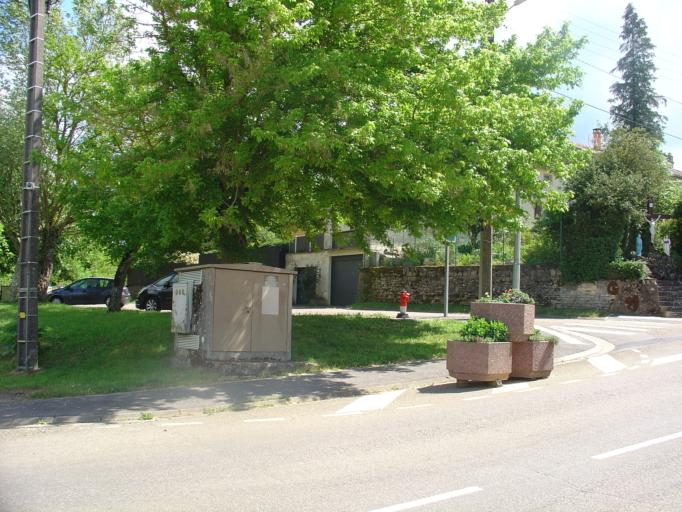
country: FR
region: Lorraine
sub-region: Departement de Meurthe-et-Moselle
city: Villey-Saint-Etienne
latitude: 48.8317
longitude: 5.9080
